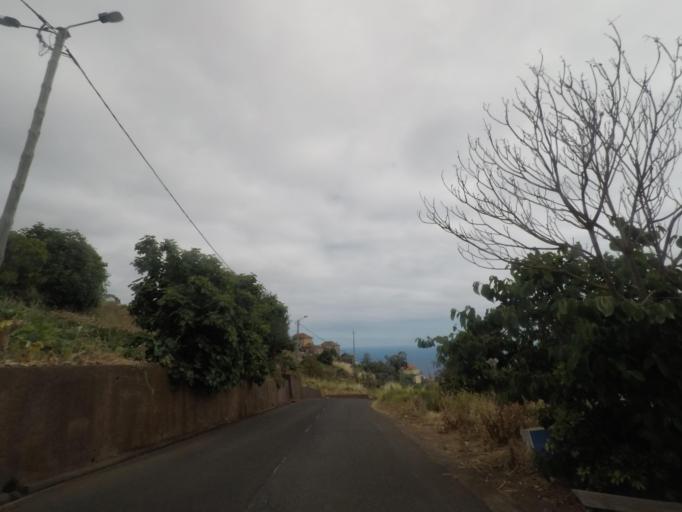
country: PT
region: Madeira
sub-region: Calheta
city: Estreito da Calheta
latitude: 32.7387
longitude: -17.1712
